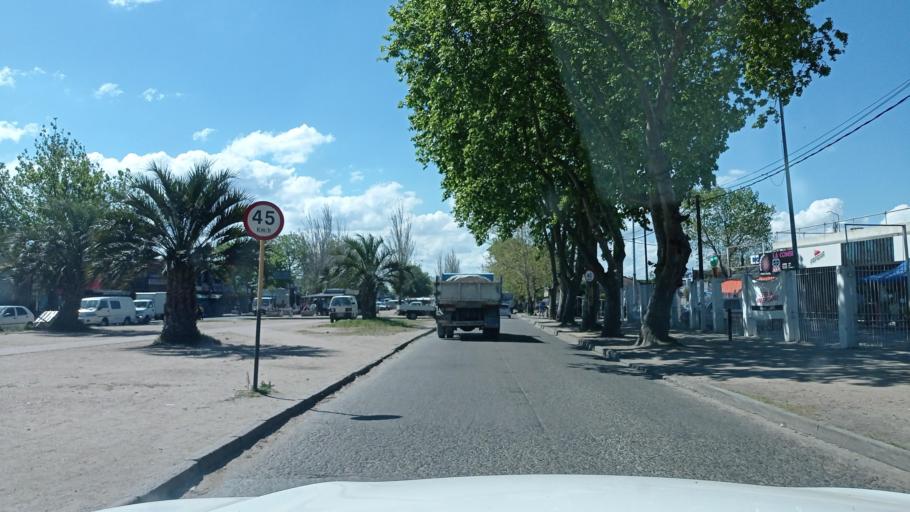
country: UY
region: Montevideo
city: Montevideo
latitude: -34.8288
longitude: -56.1408
